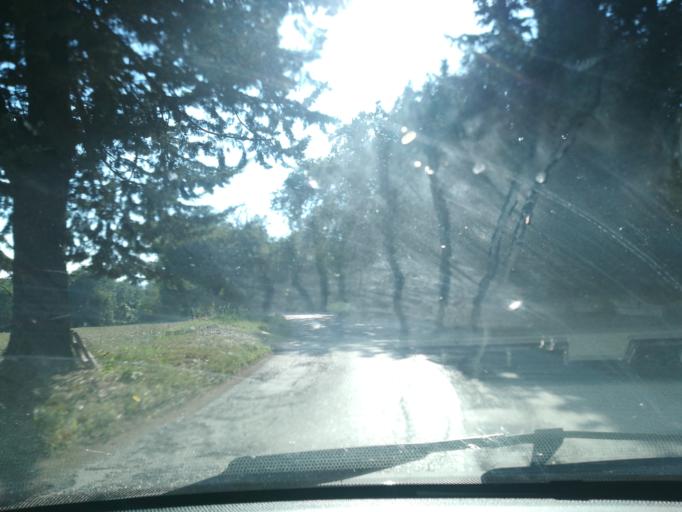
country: IT
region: The Marches
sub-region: Provincia di Macerata
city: Piediripa
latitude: 43.2853
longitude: 13.4870
